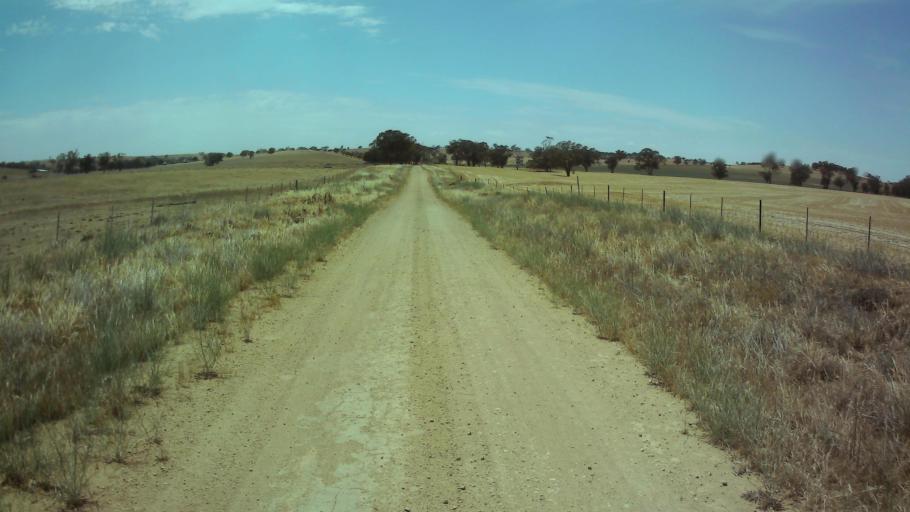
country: AU
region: New South Wales
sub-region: Cowra
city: Cowra
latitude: -33.9573
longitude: 148.4415
